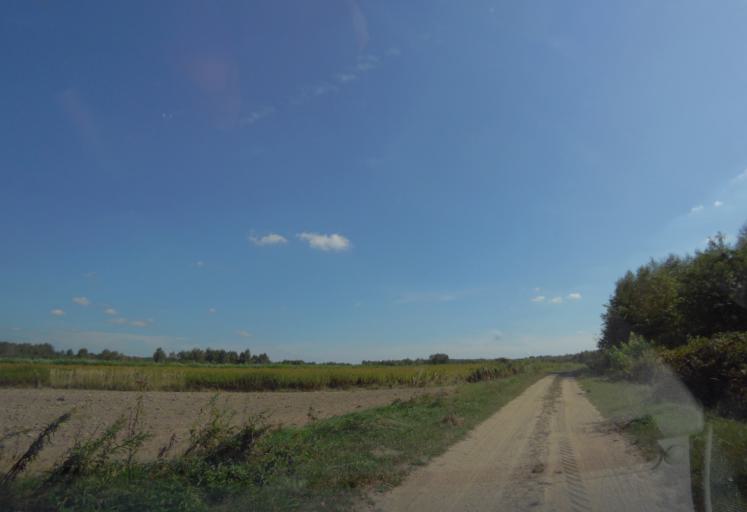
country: PL
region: Subcarpathian Voivodeship
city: Nowa Sarzyna
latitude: 50.2975
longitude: 22.3192
